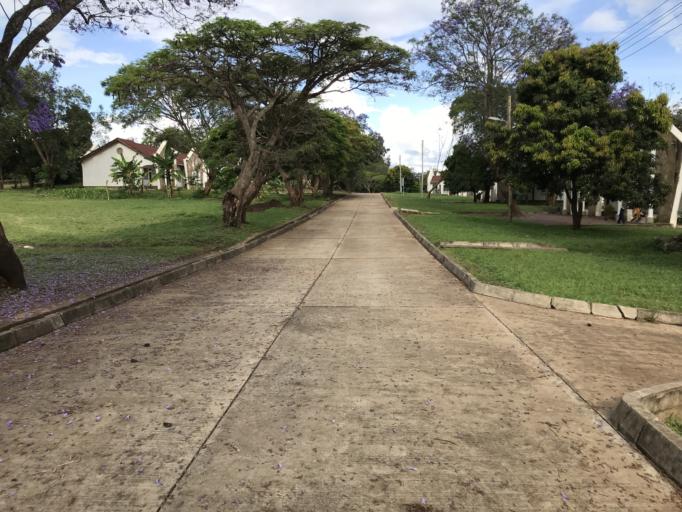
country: TZ
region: Arusha
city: Usa River
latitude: -3.4000
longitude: 36.7987
